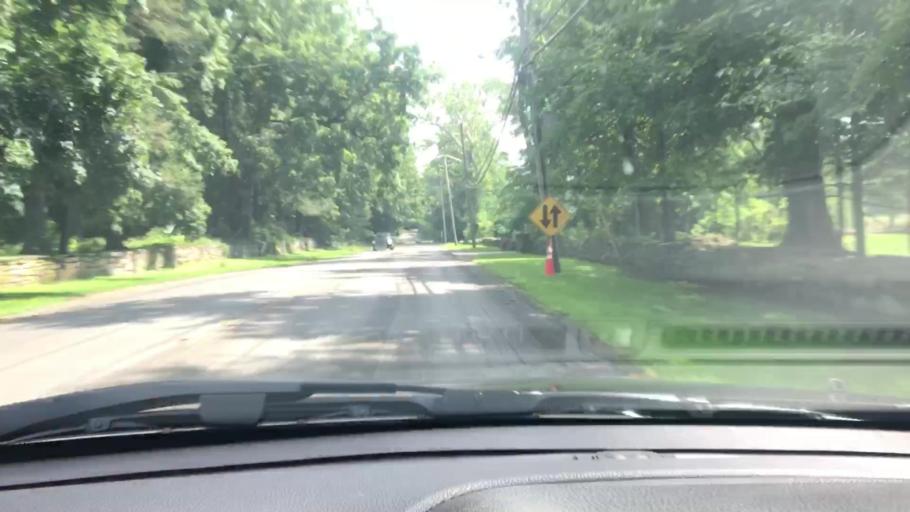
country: US
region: New York
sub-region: Westchester County
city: Bedford
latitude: 41.2129
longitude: -73.6513
